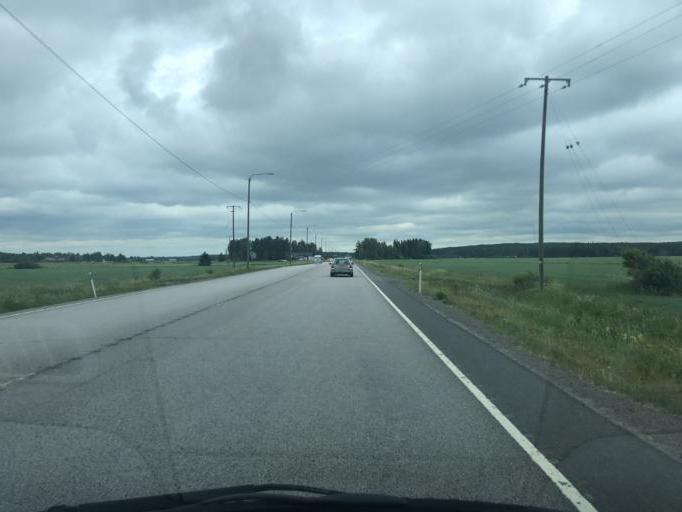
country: FI
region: Uusimaa
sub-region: Loviisa
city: Lapinjaervi
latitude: 60.6582
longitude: 26.2423
